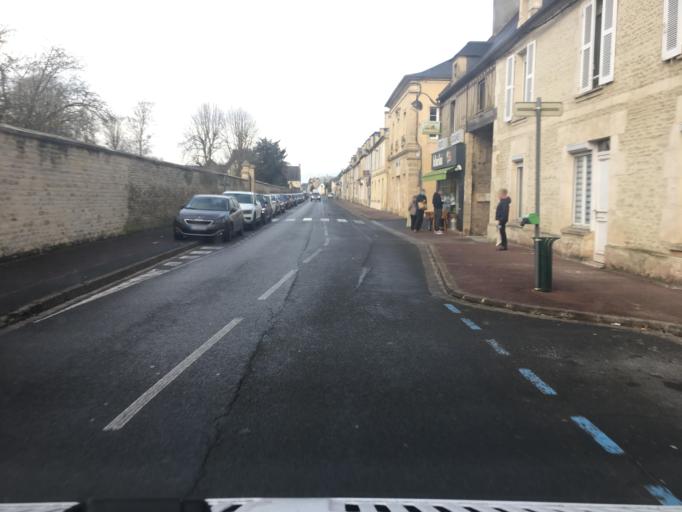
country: FR
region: Lower Normandy
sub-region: Departement du Calvados
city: Saint-Manvieu
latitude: 49.2104
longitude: -0.5118
